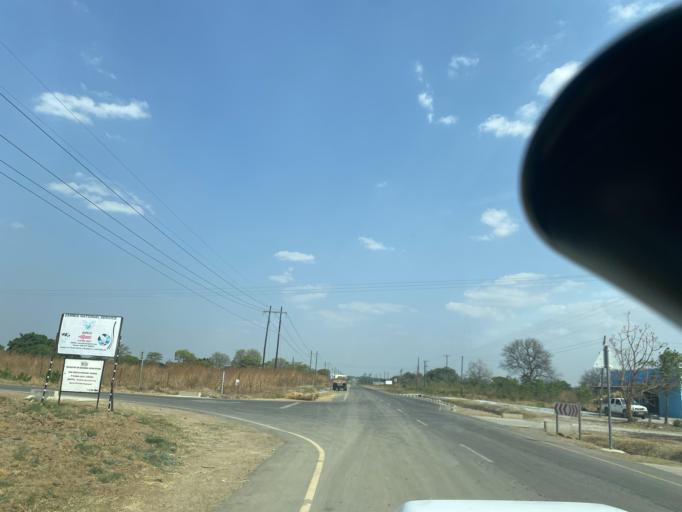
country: ZM
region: Lusaka
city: Lusaka
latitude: -15.3181
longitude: 28.0614
